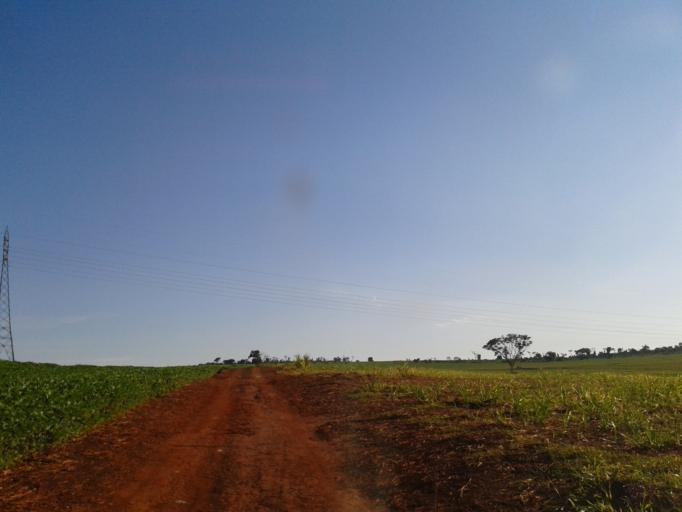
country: BR
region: Minas Gerais
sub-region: Centralina
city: Centralina
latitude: -18.6777
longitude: -49.2754
